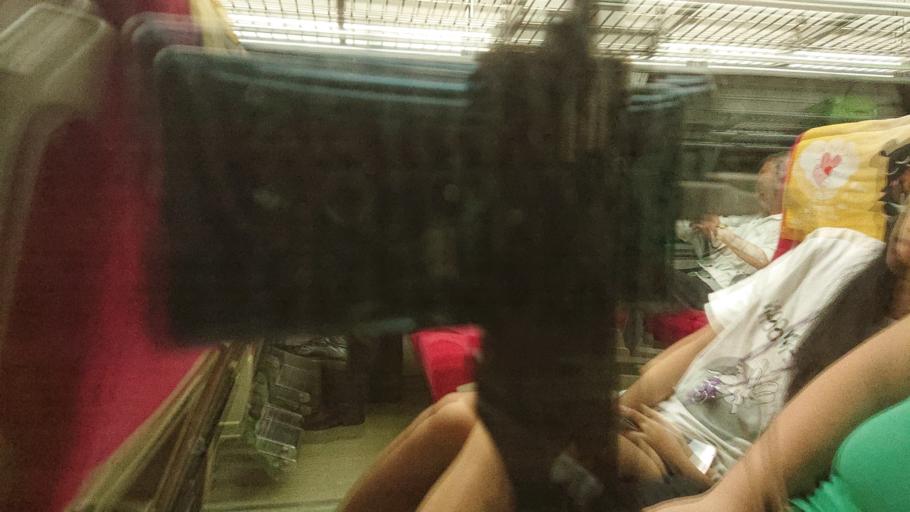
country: TW
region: Taiwan
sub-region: Keelung
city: Keelung
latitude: 25.0925
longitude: 121.8306
